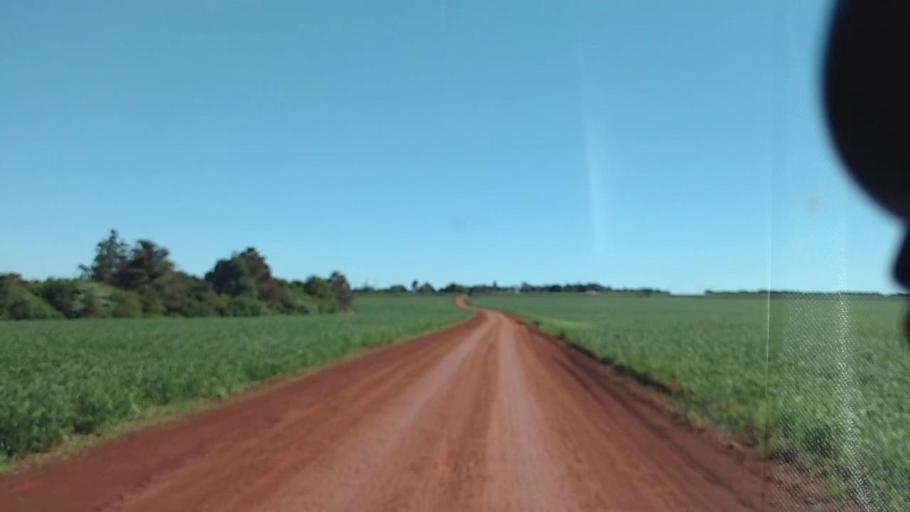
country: PY
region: Alto Parana
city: Naranjal
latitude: -25.9487
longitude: -55.1132
